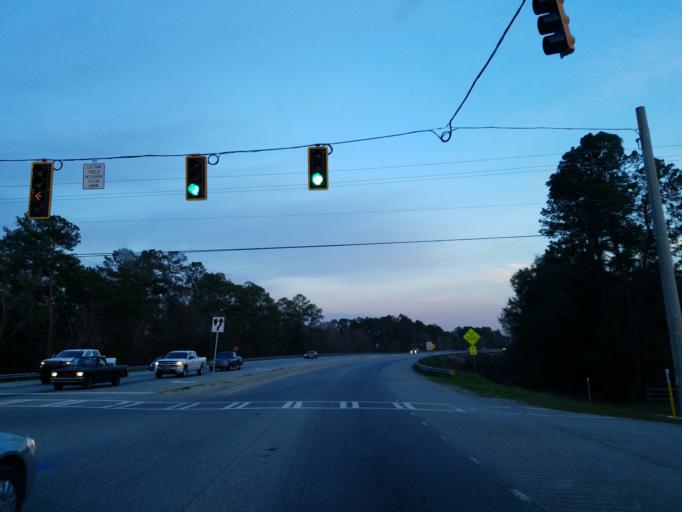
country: US
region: Georgia
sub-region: Lowndes County
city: Remerton
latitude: 30.8528
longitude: -83.3447
